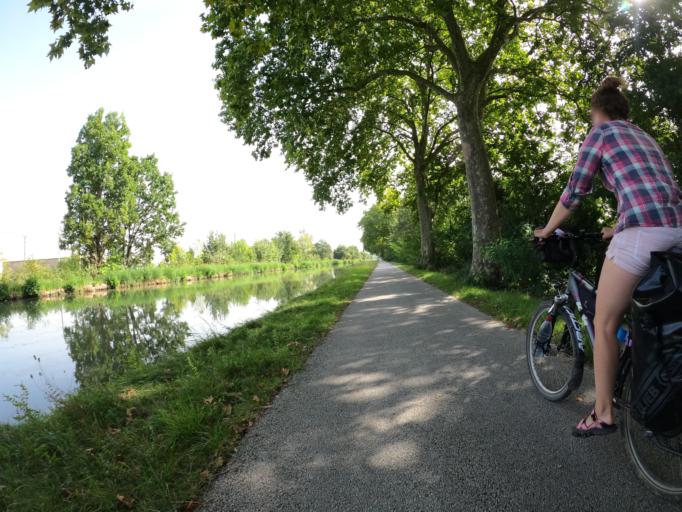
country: FR
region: Midi-Pyrenees
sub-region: Departement de la Haute-Garonne
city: Lespinasse
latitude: 43.7213
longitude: 1.3806
